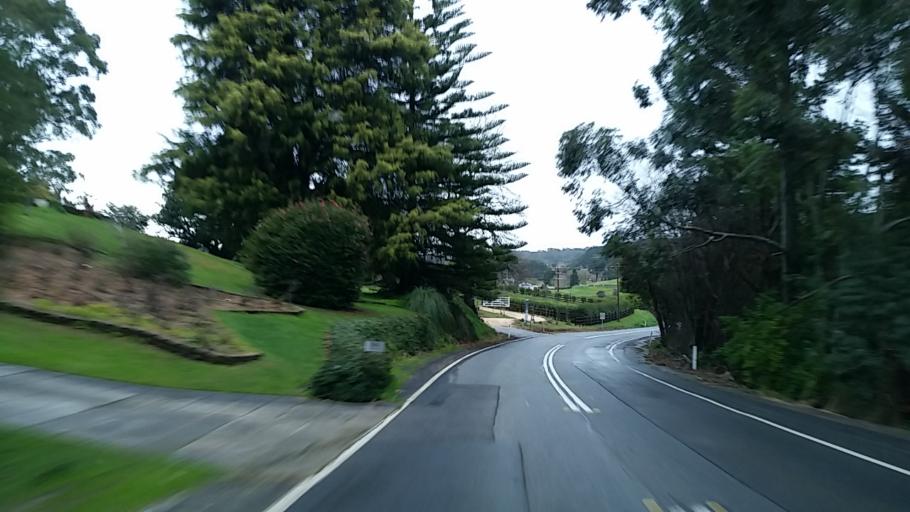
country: AU
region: South Australia
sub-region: Adelaide Hills
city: Bridgewater
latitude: -34.9635
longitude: 138.7354
